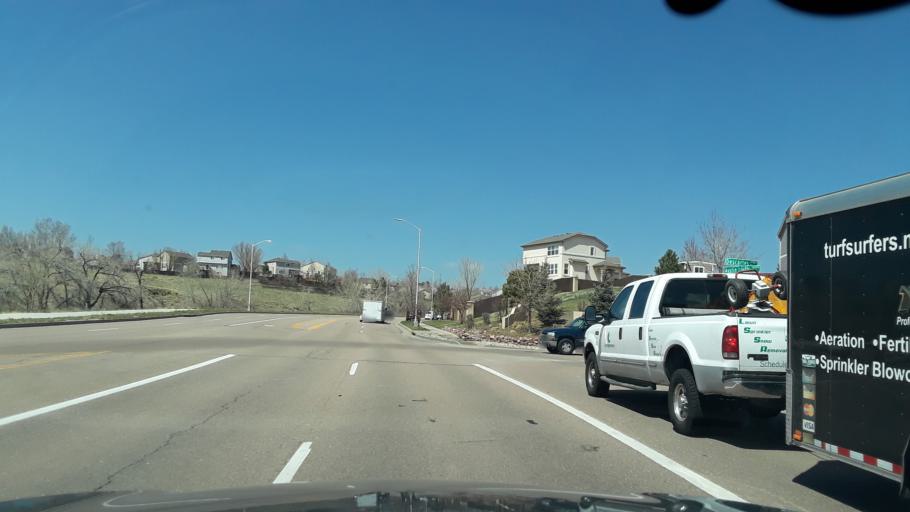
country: US
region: Colorado
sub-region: El Paso County
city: Black Forest
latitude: 38.9420
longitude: -104.7401
